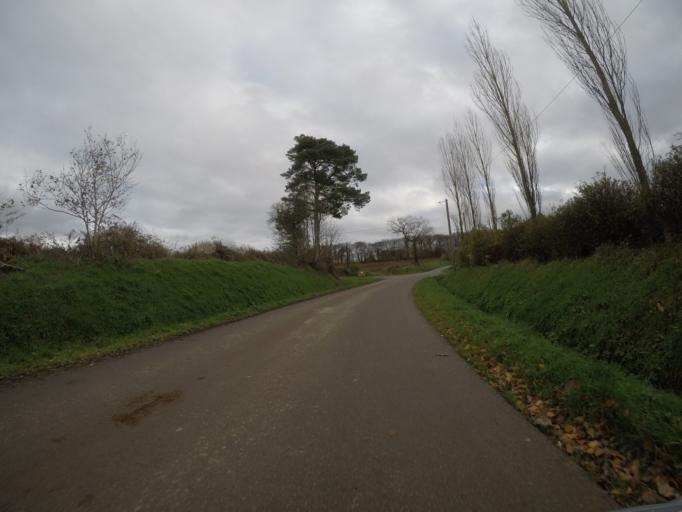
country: FR
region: Brittany
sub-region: Departement des Cotes-d'Armor
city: Callac
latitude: 48.4082
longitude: -3.3855
